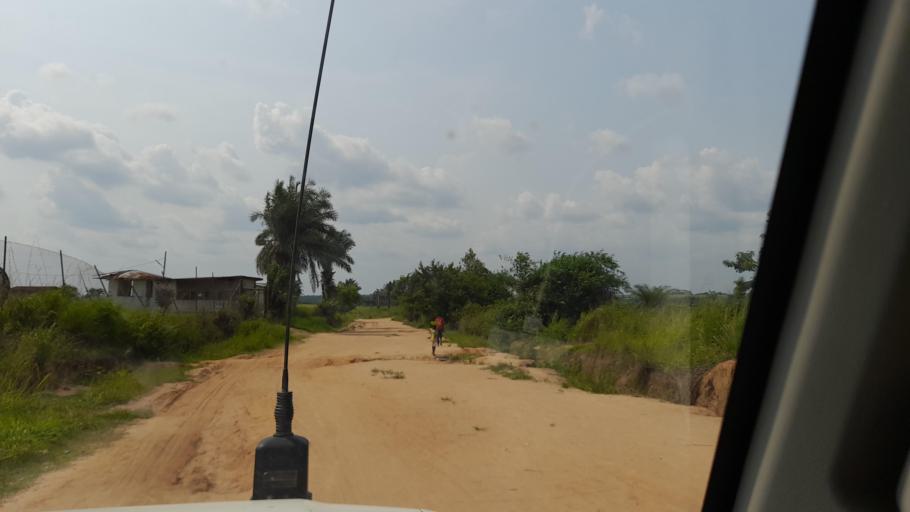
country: CD
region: Kasai-Occidental
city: Kananga
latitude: -5.9148
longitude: 22.4784
